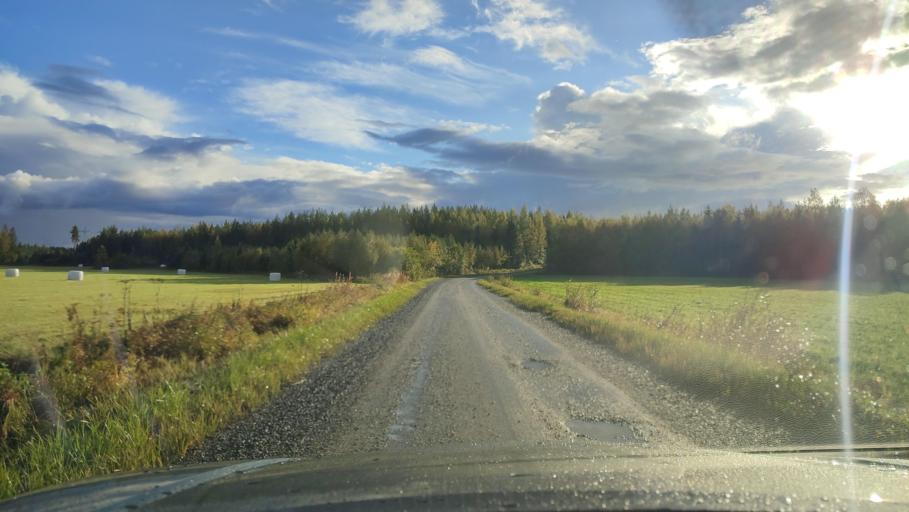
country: FI
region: Southern Ostrobothnia
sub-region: Suupohja
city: Karijoki
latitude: 62.3099
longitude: 21.5468
